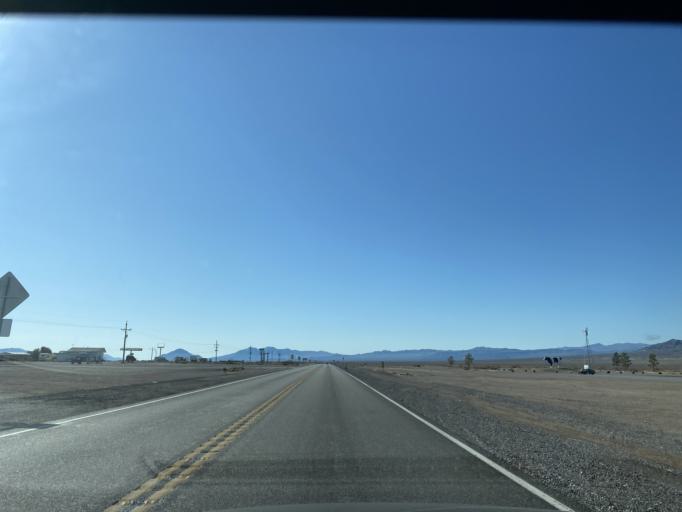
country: US
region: Nevada
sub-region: Nye County
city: Pahrump
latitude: 36.4130
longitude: -116.4223
